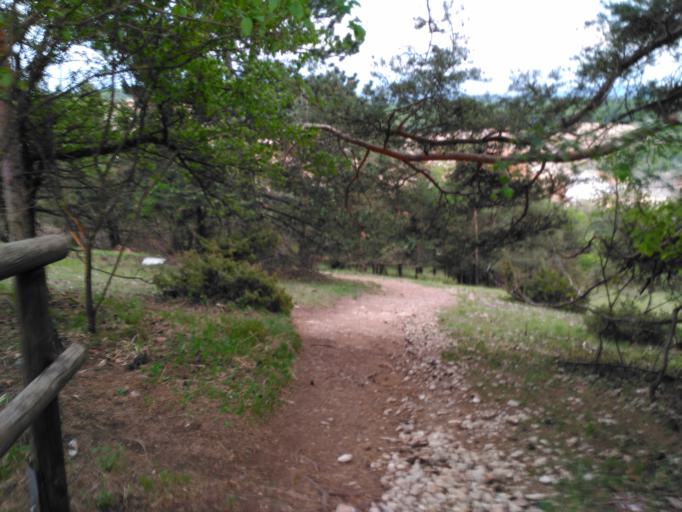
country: CZ
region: Central Bohemia
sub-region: Okres Beroun
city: Kraluv Dvur
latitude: 49.9143
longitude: 14.0646
